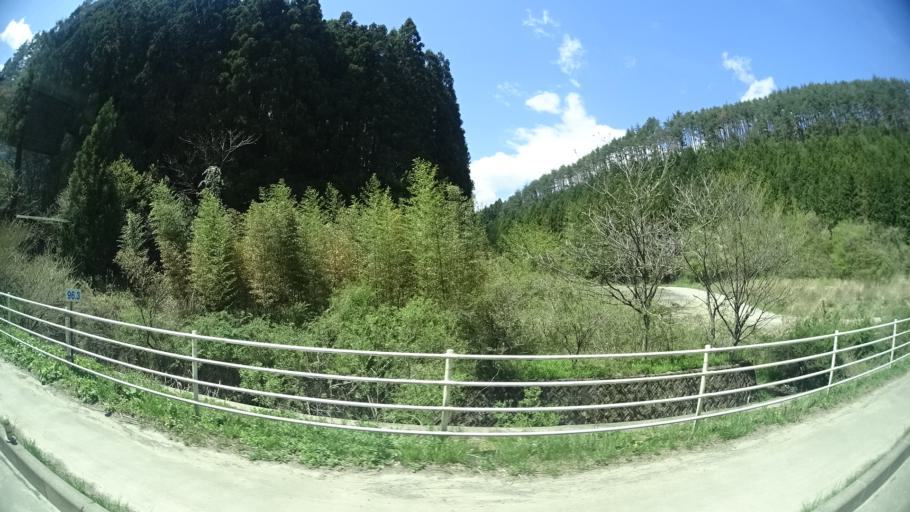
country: JP
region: Miyagi
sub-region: Oshika Gun
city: Onagawa Cho
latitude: 38.6960
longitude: 141.4742
